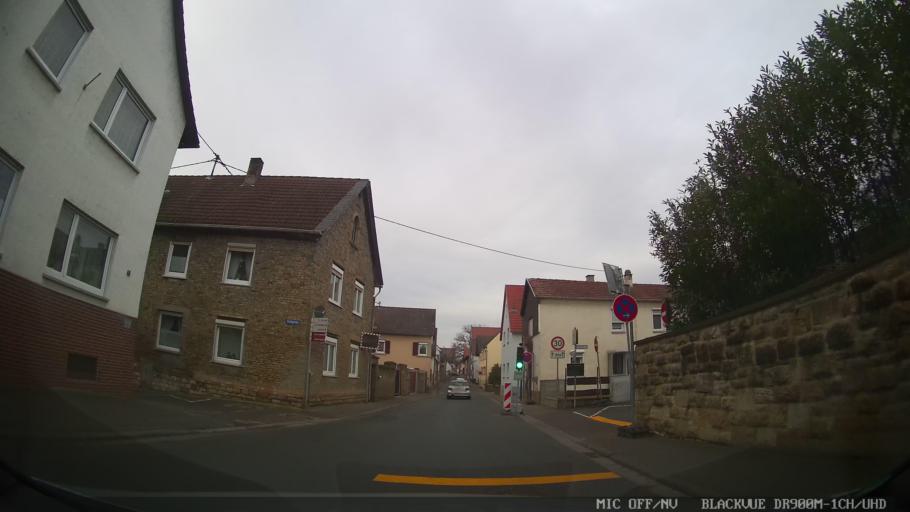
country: DE
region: Rheinland-Pfalz
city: Selzen
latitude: 49.8617
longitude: 8.2552
